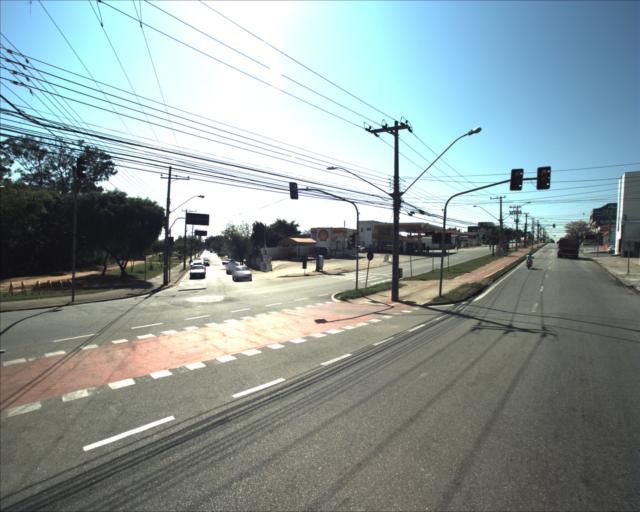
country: BR
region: Sao Paulo
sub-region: Sorocaba
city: Sorocaba
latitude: -23.5031
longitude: -47.5216
